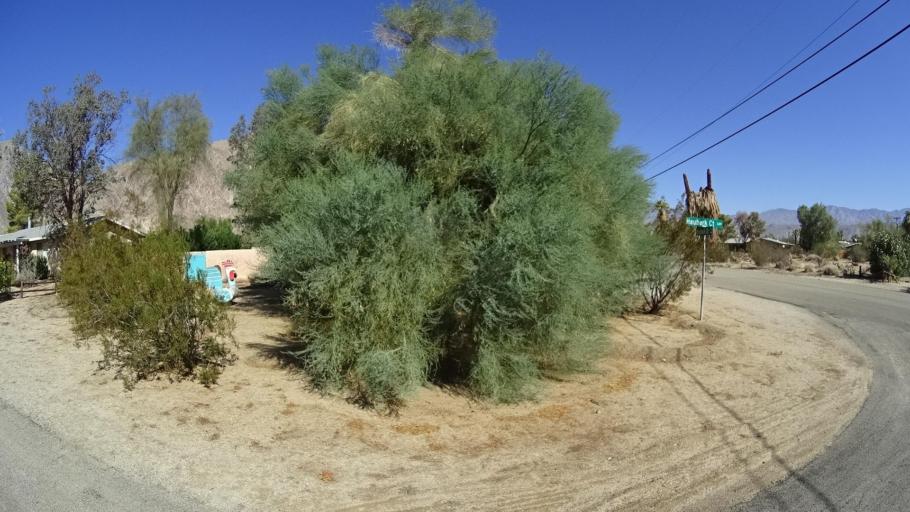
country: US
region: California
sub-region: San Diego County
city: Borrego Springs
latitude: 33.2738
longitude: -116.3937
